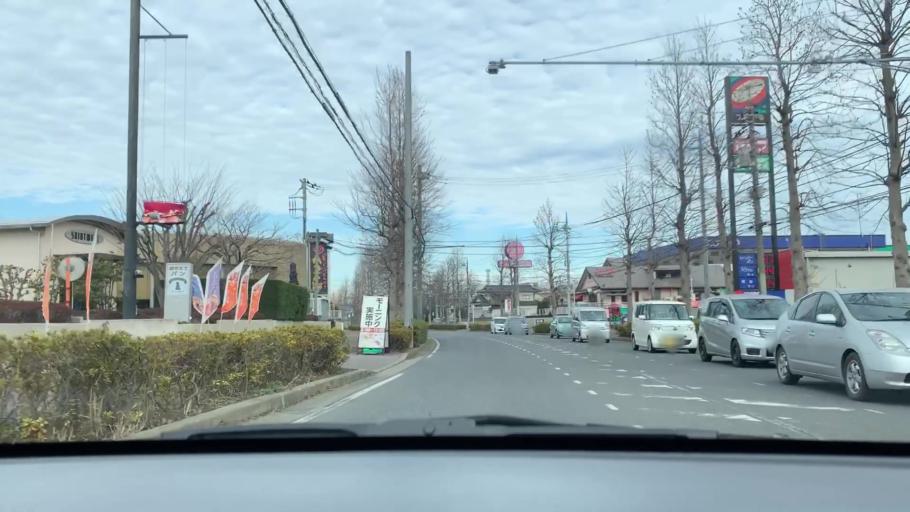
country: JP
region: Chiba
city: Kashiwa
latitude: 35.8892
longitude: 139.9451
